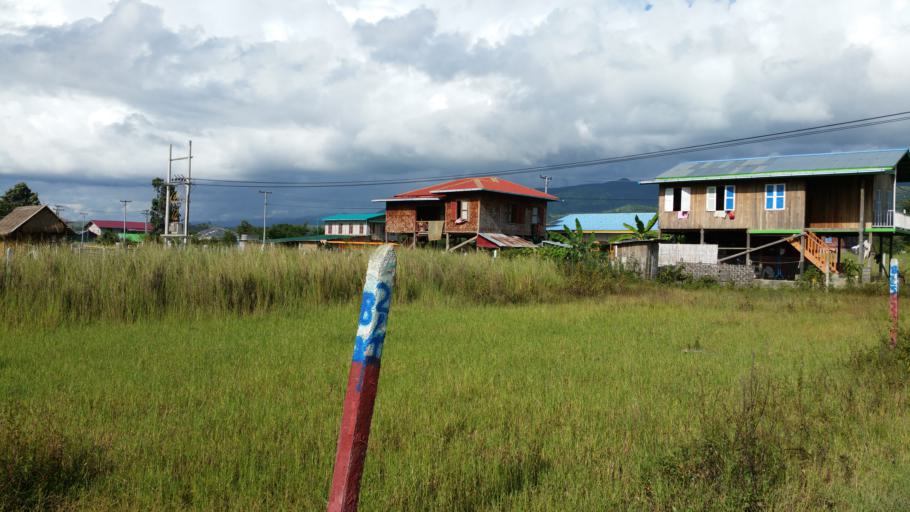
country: MM
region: Shan
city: Taunggyi
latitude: 20.6658
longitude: 96.9449
